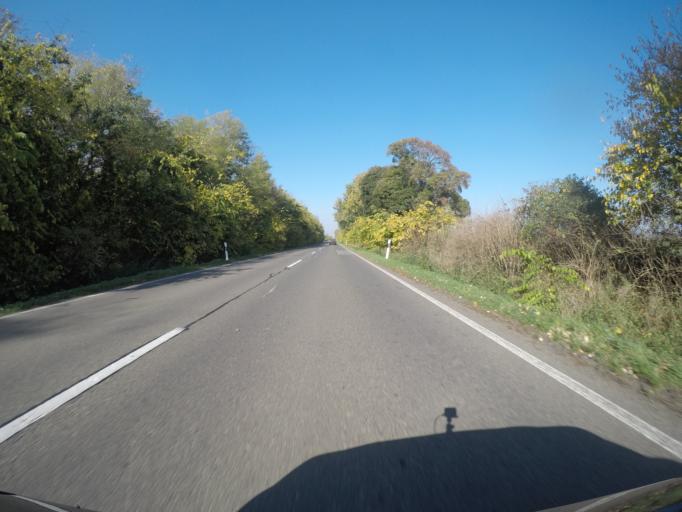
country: HU
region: Tolna
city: Szedres
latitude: 46.5202
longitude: 18.6615
